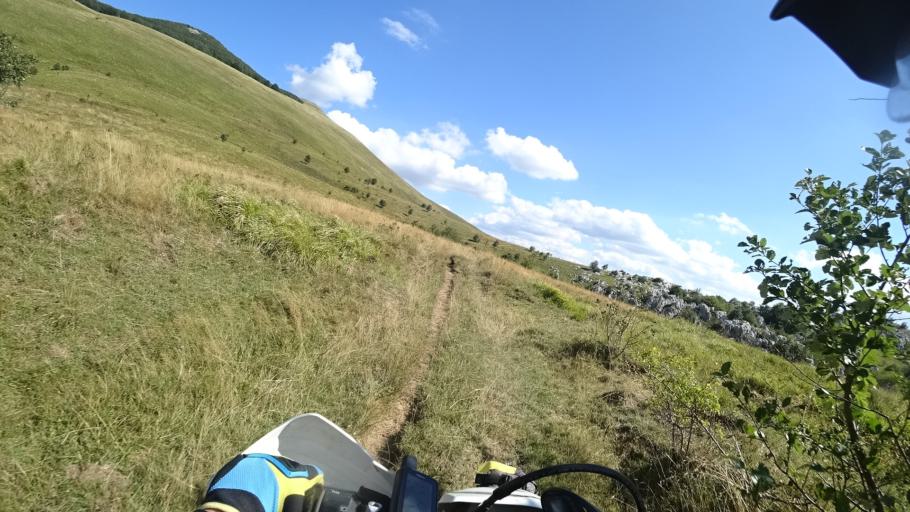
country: HR
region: Zadarska
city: Gracac
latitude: 44.4074
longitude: 16.0027
